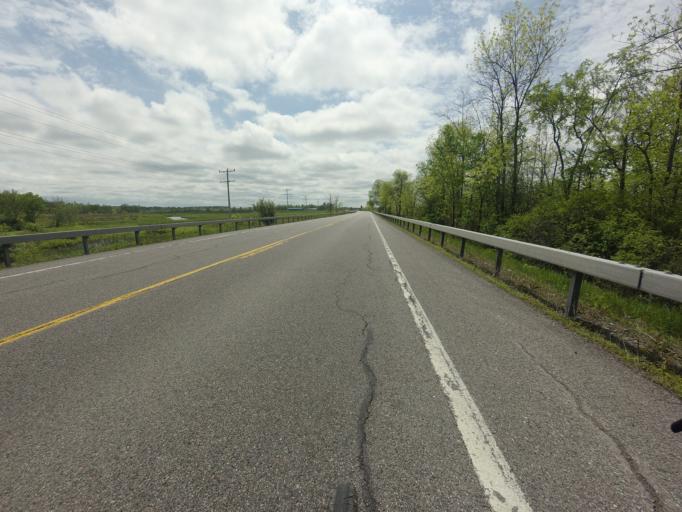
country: CA
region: Ontario
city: Cornwall
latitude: 44.9594
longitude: -74.6694
